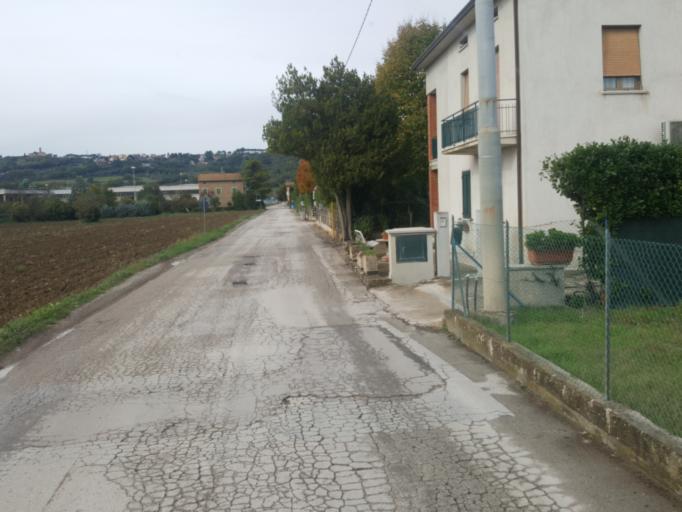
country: IT
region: Umbria
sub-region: Provincia di Perugia
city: San Martino in Campo
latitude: 43.0693
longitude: 12.4232
